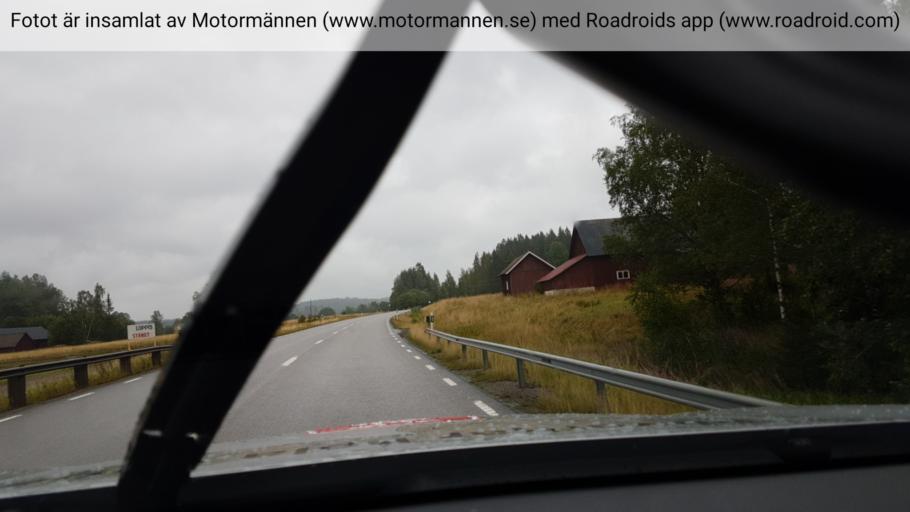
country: SE
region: Vaestra Goetaland
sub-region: Bengtsfors Kommun
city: Billingsfors
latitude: 58.9417
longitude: 12.2136
